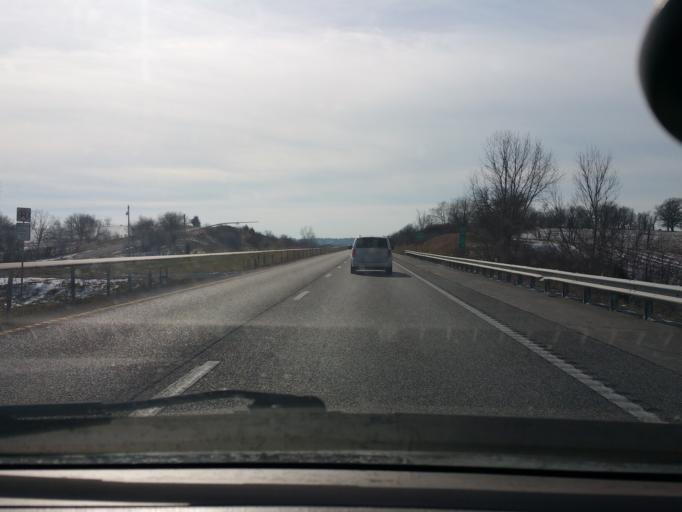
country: US
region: Missouri
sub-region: Clay County
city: Liberty
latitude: 39.2971
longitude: -94.4105
